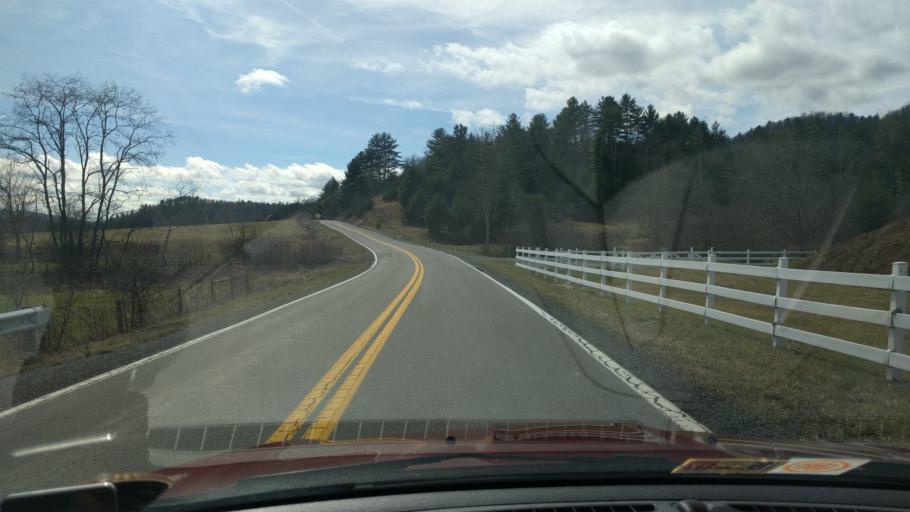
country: US
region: West Virginia
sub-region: Pocahontas County
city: Marlinton
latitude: 38.2208
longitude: -79.9204
